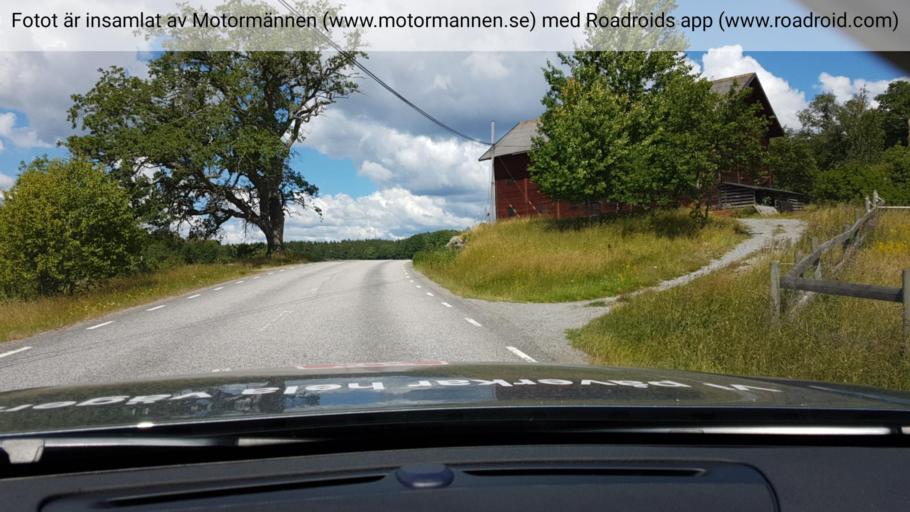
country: SE
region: Stockholm
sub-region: Varmdo Kommun
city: Hemmesta
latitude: 59.3733
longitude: 18.5271
